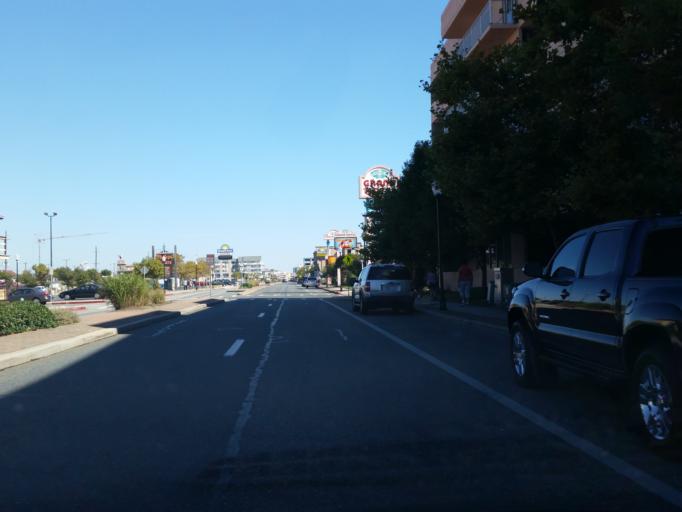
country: US
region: Maryland
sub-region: Worcester County
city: Ocean City
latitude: 38.3498
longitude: -75.0769
